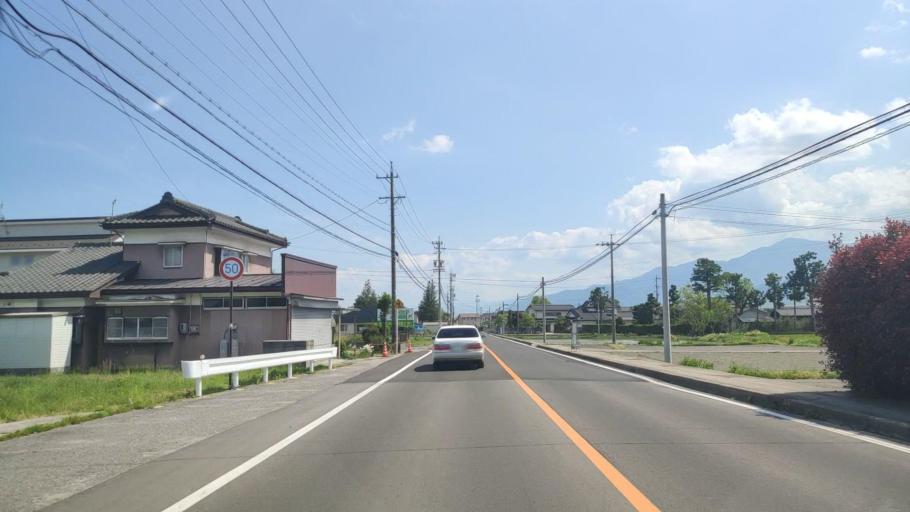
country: JP
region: Nagano
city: Hotaka
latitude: 36.4032
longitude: 137.8614
